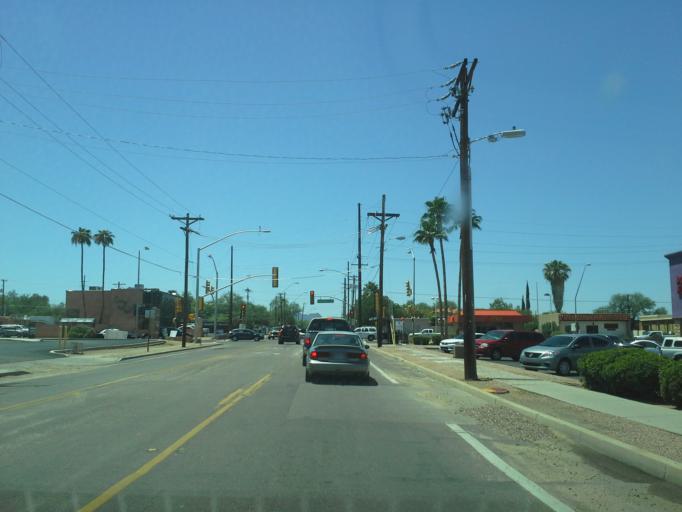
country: US
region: Arizona
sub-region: Pima County
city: Tucson
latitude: 32.2576
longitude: -110.9430
